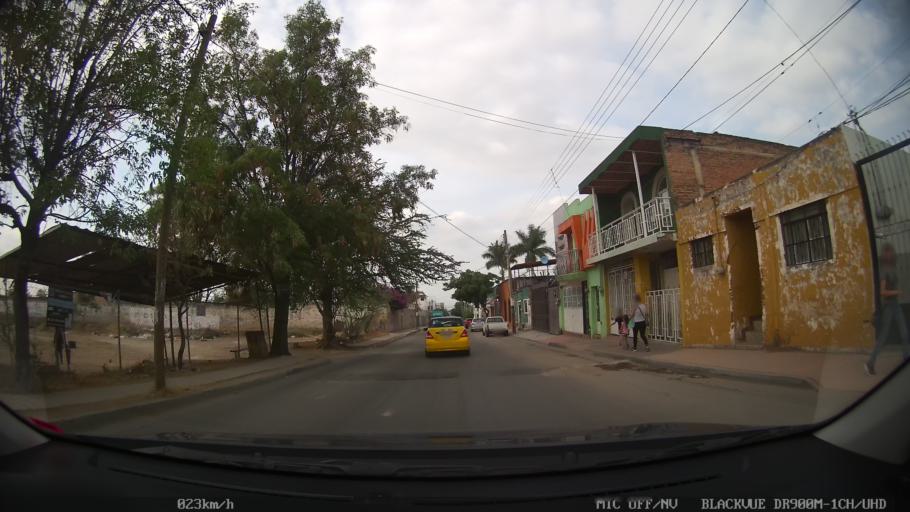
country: MX
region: Jalisco
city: Tonala
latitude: 20.6286
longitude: -103.2371
